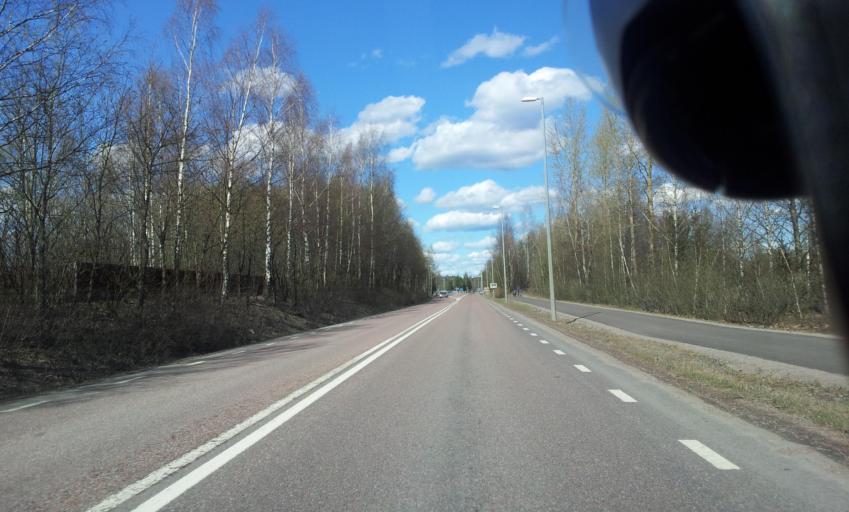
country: SE
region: Dalarna
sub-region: Faluns Kommun
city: Falun
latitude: 60.6134
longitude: 15.6153
